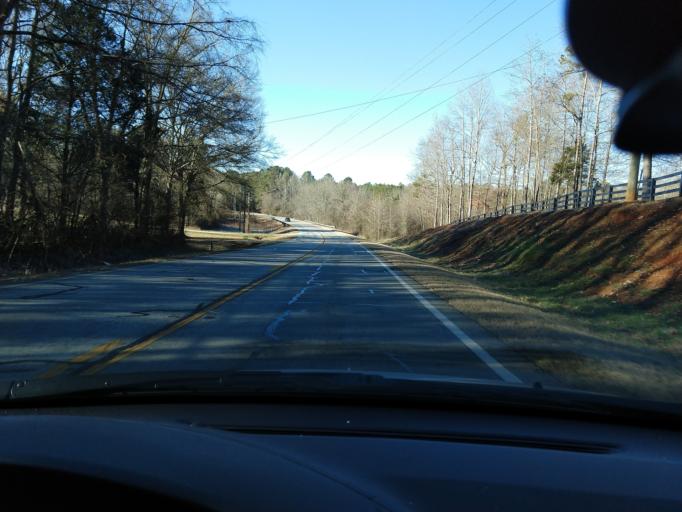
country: US
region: Georgia
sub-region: Jackson County
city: Jefferson
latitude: 34.1536
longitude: -83.5172
